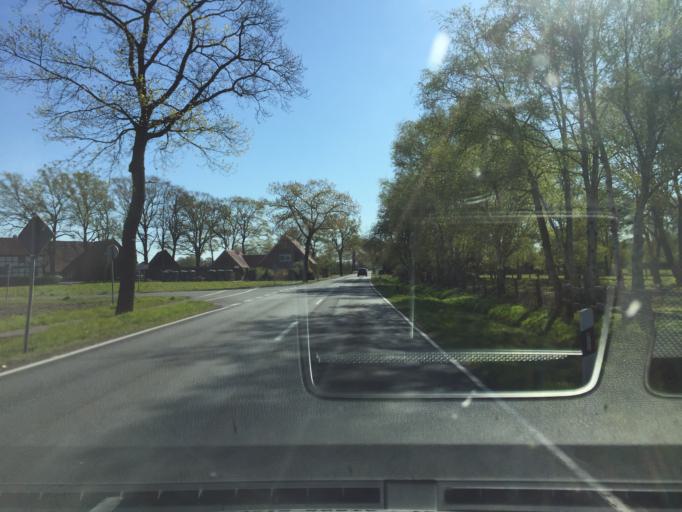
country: DE
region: Lower Saxony
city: Wagenfeld
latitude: 52.5480
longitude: 8.5997
